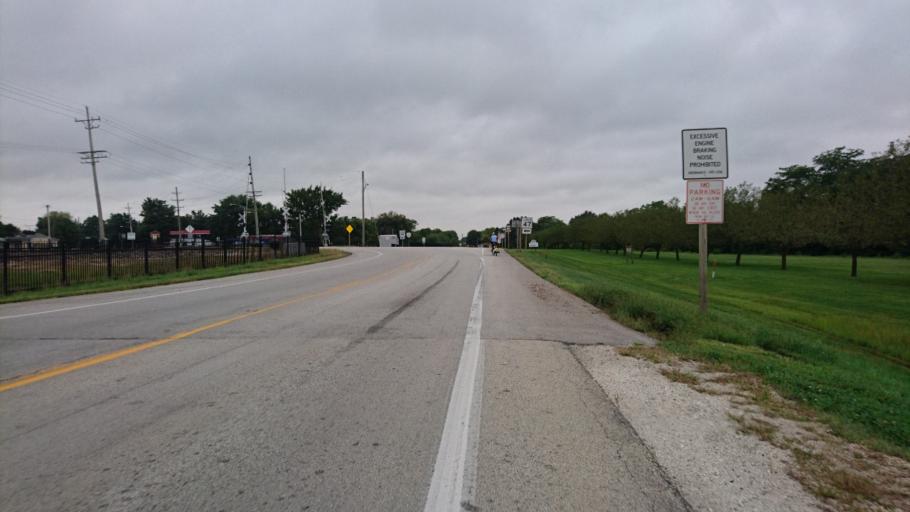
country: US
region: Illinois
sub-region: Livingston County
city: Dwight
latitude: 41.0991
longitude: -88.4201
